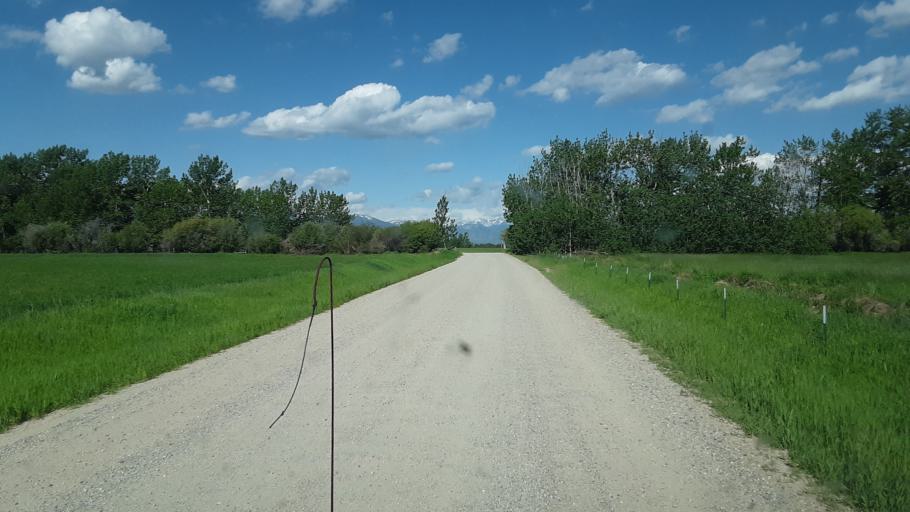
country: US
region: Montana
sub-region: Carbon County
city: Red Lodge
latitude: 45.2787
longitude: -109.1958
